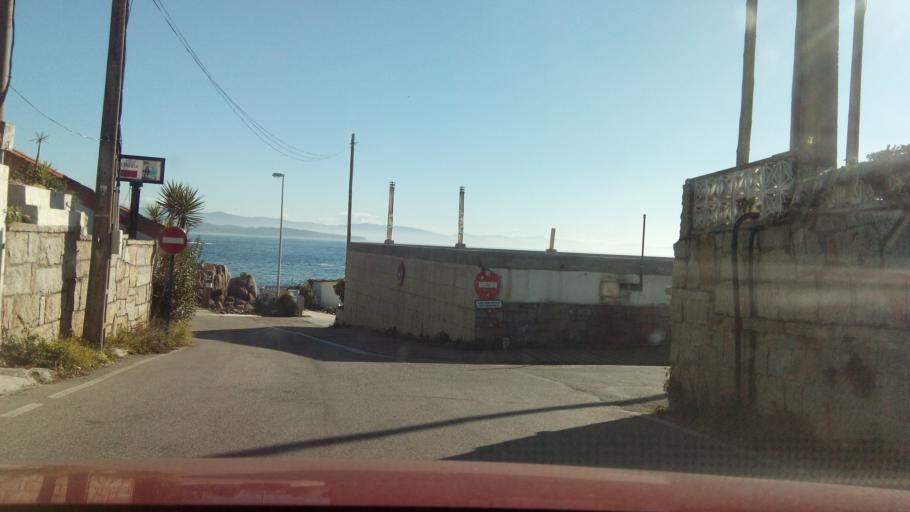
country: ES
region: Galicia
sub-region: Provincia de Pontevedra
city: O Grove
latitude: 42.4540
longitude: -8.9246
